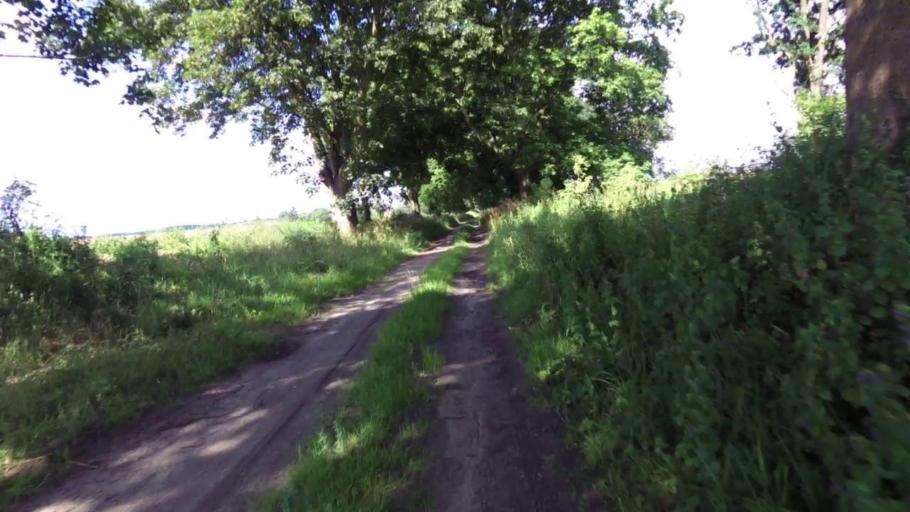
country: PL
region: West Pomeranian Voivodeship
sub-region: Powiat stargardzki
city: Stargard Szczecinski
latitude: 53.3474
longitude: 15.1006
